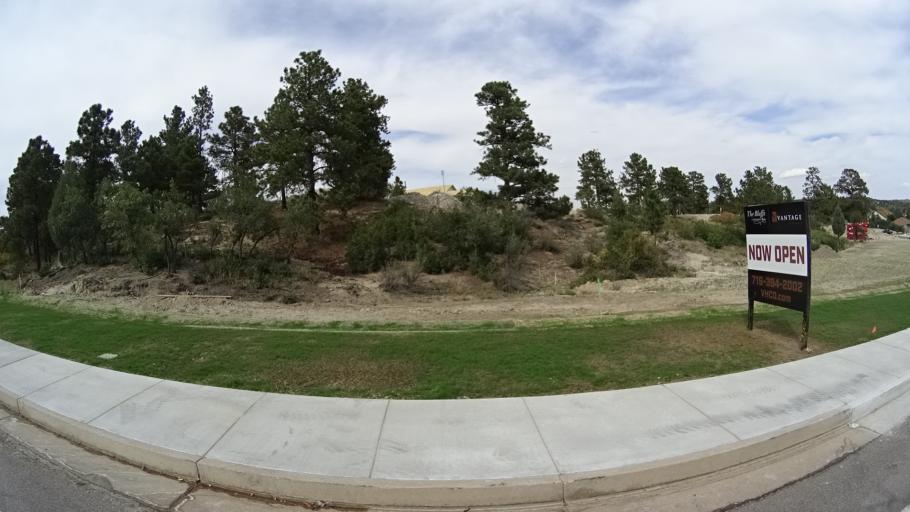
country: US
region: Colorado
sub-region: El Paso County
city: Colorado Springs
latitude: 38.9022
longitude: -104.7893
